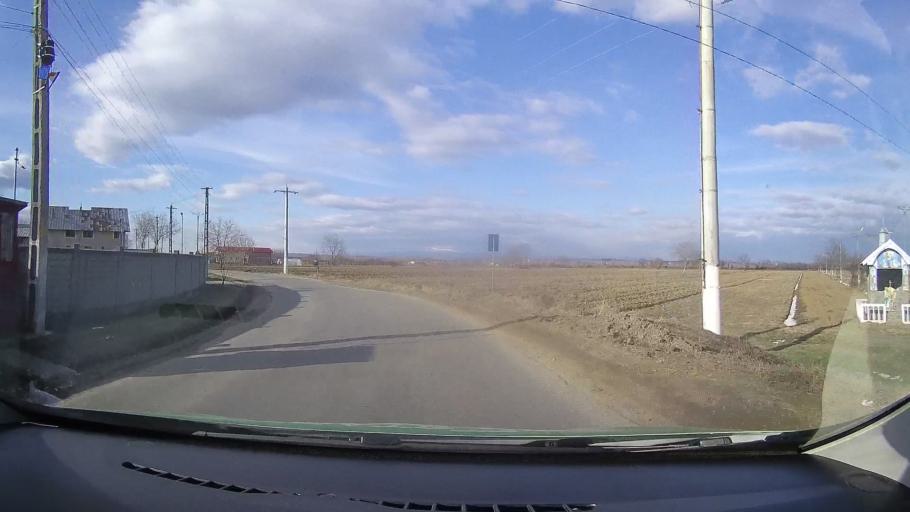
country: RO
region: Dambovita
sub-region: Comuna Ulmi
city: Ulmi
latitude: 44.8930
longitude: 25.5039
